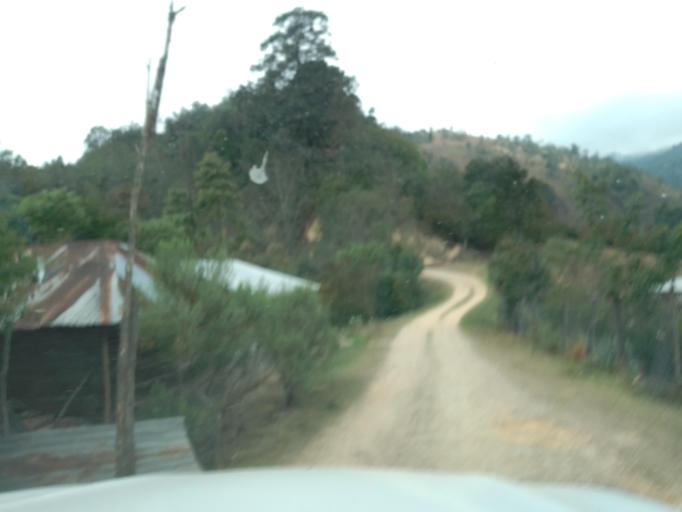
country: GT
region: San Marcos
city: Tacana
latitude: 15.2193
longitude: -92.2131
